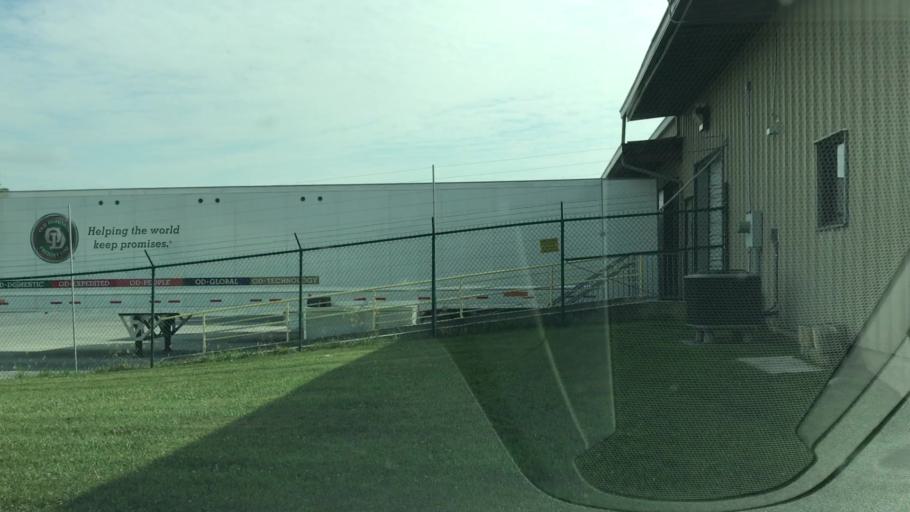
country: US
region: Virginia
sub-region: City of Winchester
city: Winchester
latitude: 39.2223
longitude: -78.1472
